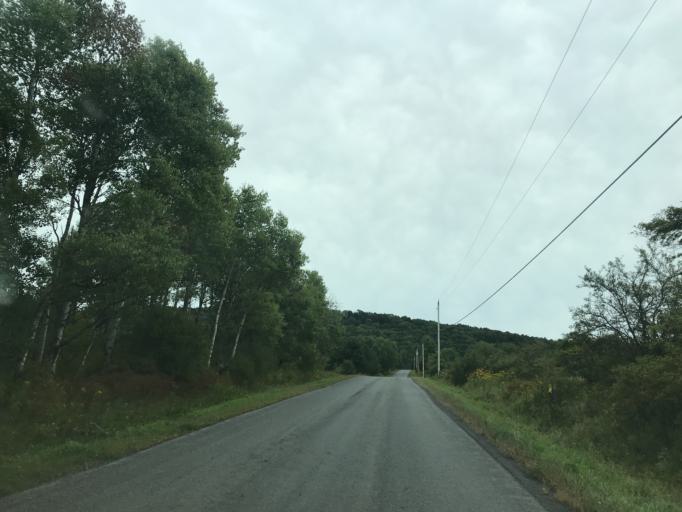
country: US
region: New York
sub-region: Otsego County
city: Worcester
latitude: 42.5431
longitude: -74.6632
